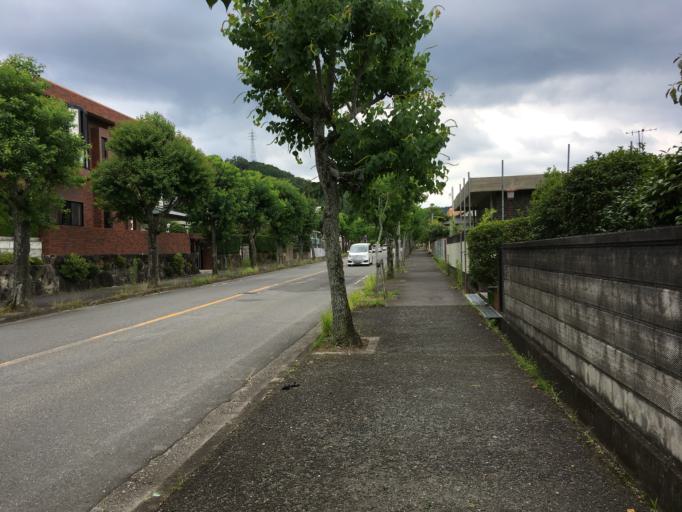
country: JP
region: Nara
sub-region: Ikoma-shi
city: Ikoma
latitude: 34.6807
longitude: 135.7174
